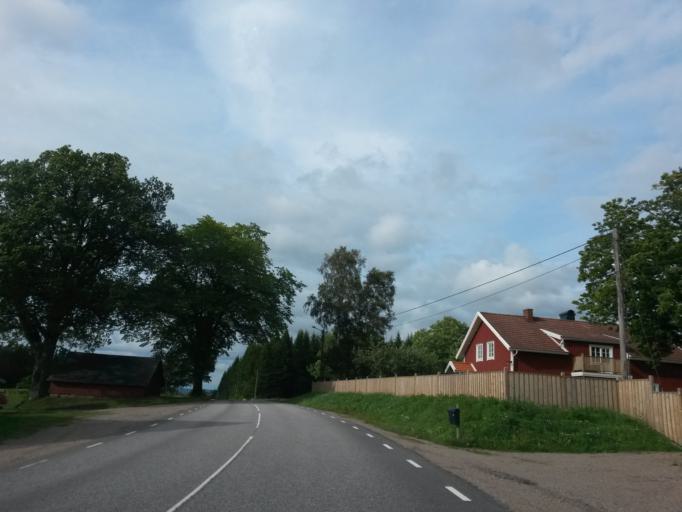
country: SE
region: Vaestra Goetaland
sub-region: Boras Kommun
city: Ganghester
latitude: 57.7821
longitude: 13.0251
